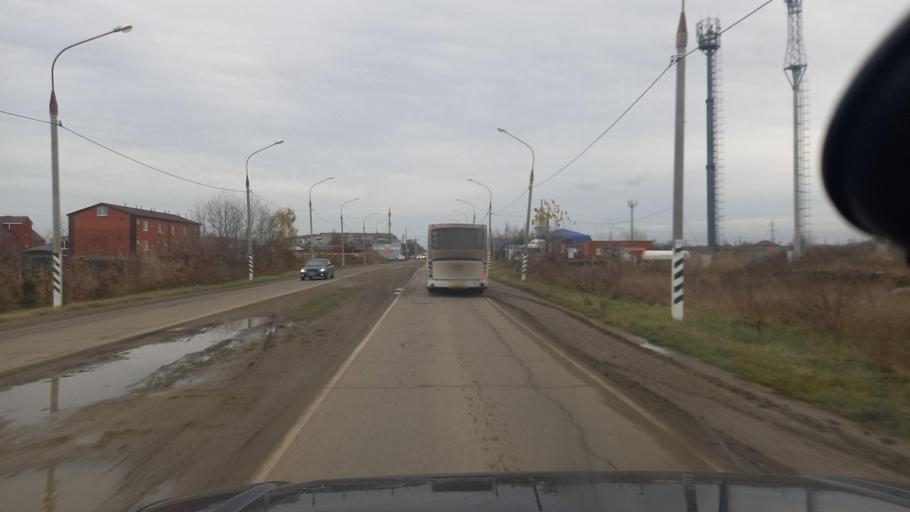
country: RU
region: Adygeya
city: Yablonovskiy
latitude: 44.9803
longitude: 38.9275
